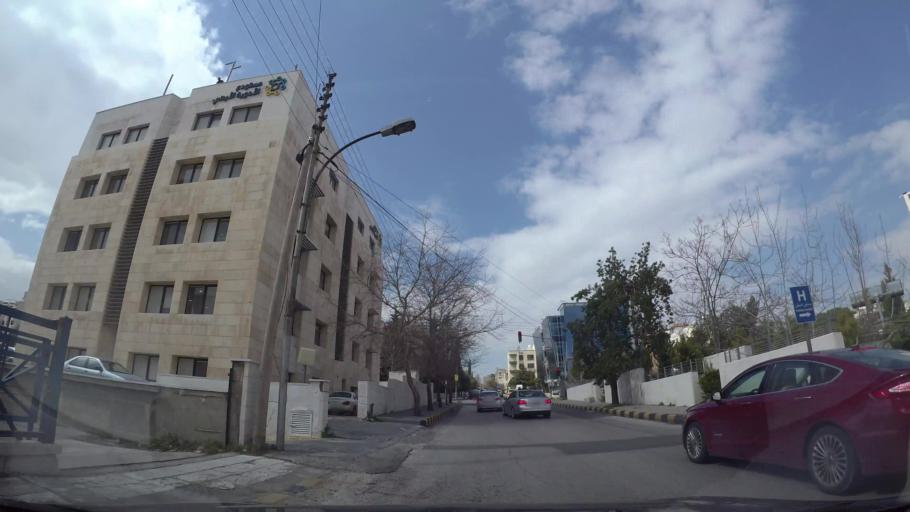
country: JO
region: Amman
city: Amman
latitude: 31.9699
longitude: 35.9043
